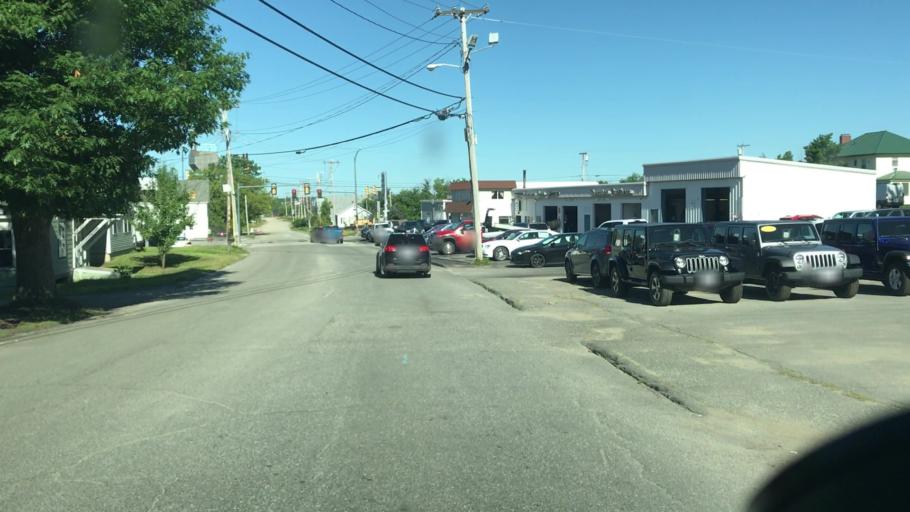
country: US
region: Maine
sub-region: Penobscot County
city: Lincoln
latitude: 45.3675
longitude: -68.5017
